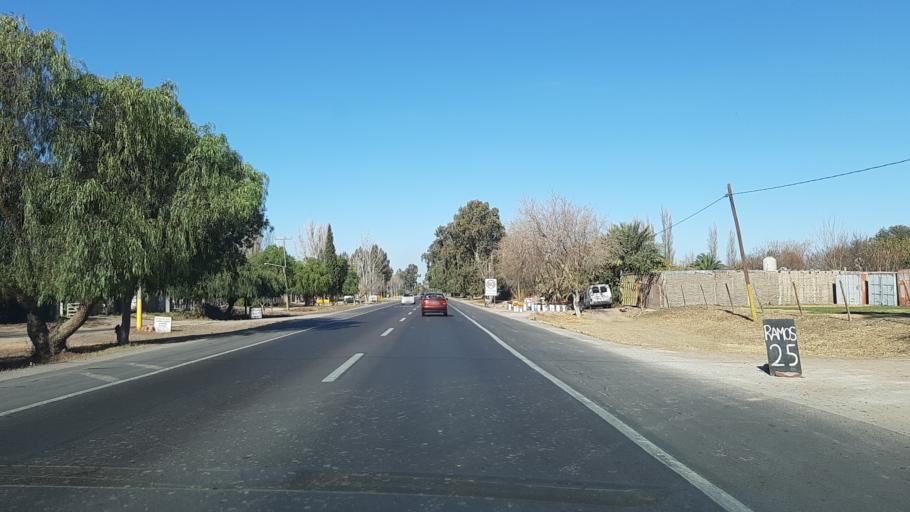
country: AR
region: San Juan
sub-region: Departamento de Santa Lucia
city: Santa Lucia
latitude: -31.5658
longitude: -68.4492
